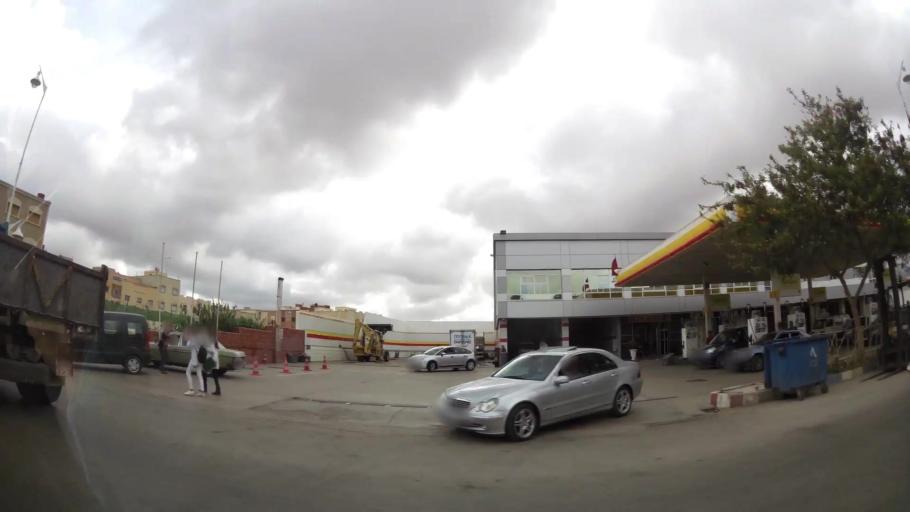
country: MA
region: Oriental
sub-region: Nador
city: Nador
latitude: 35.1581
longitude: -2.9302
